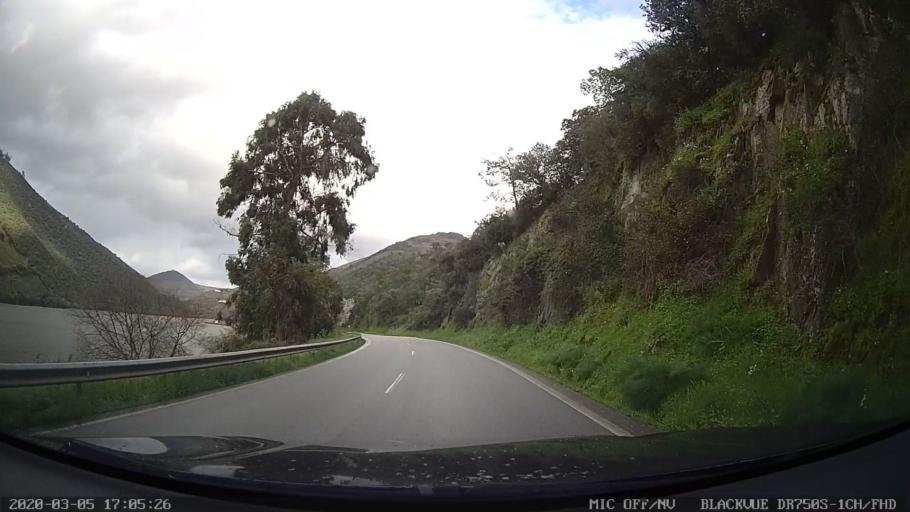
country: PT
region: Viseu
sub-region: Tabuaco
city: Tabuaco
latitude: 41.1542
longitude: -7.5922
